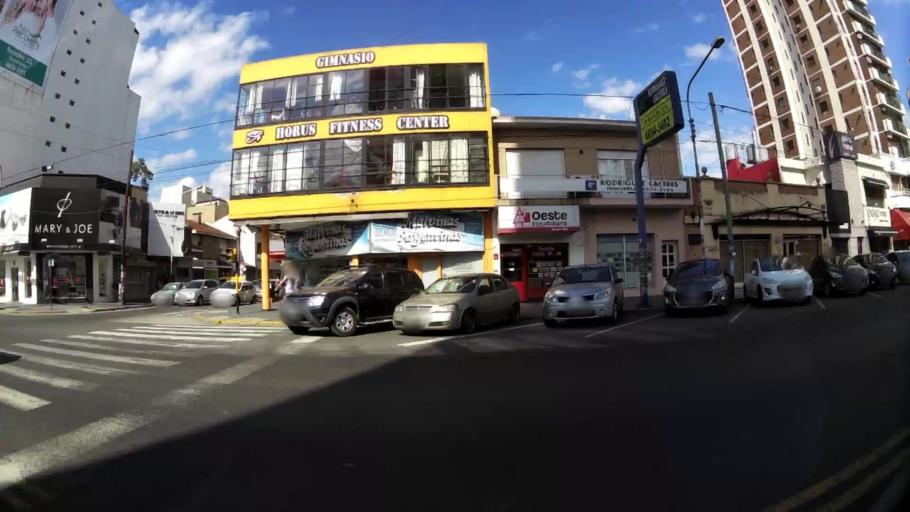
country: AR
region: Buenos Aires
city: San Justo
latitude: -34.6464
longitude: -58.5645
